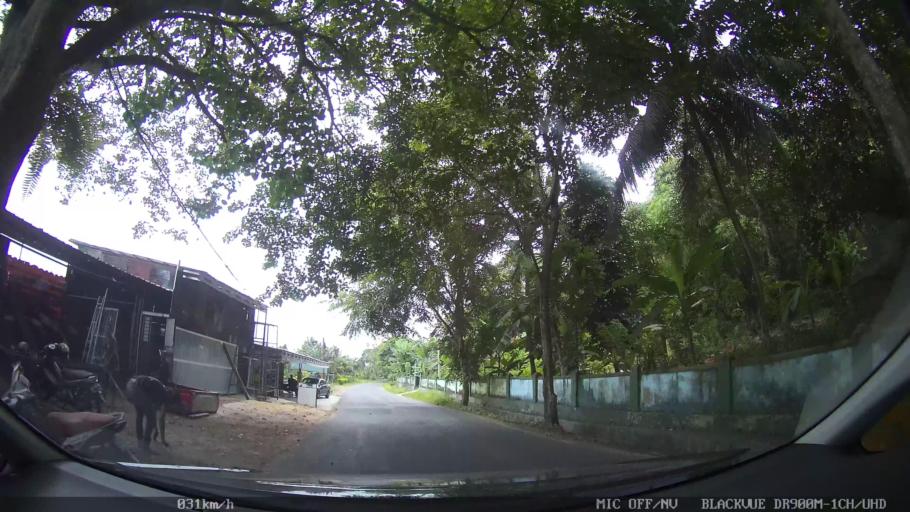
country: ID
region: Lampung
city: Bandarlampung
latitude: -5.4294
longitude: 105.2783
